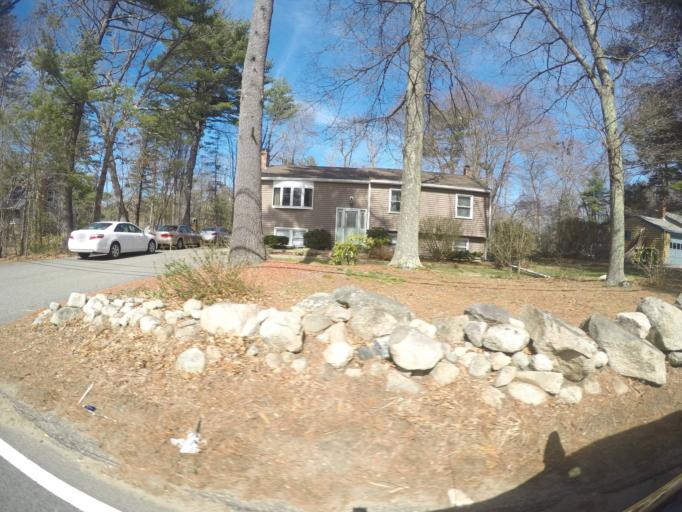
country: US
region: Massachusetts
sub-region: Bristol County
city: Easton
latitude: 42.0424
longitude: -71.0909
